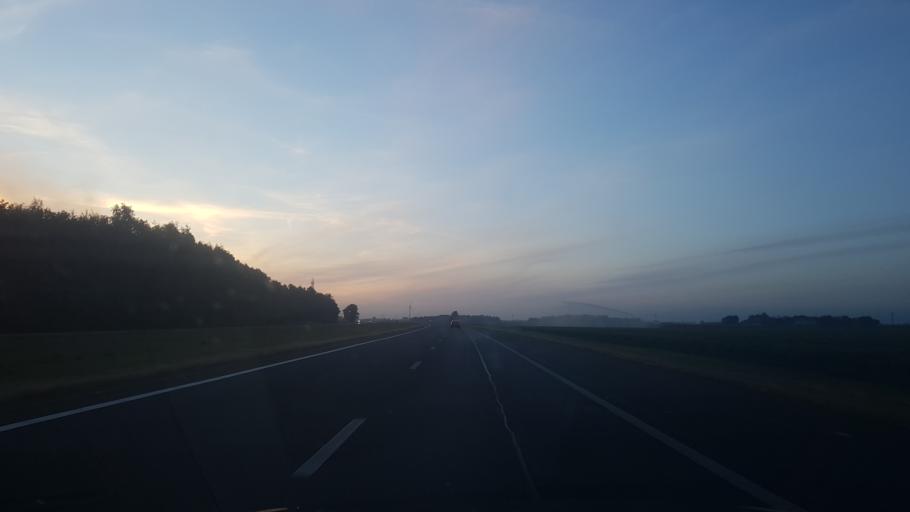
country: NL
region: Friesland
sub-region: Gemeente Lemsterland
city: Lemmer
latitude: 52.8102
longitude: 5.7471
